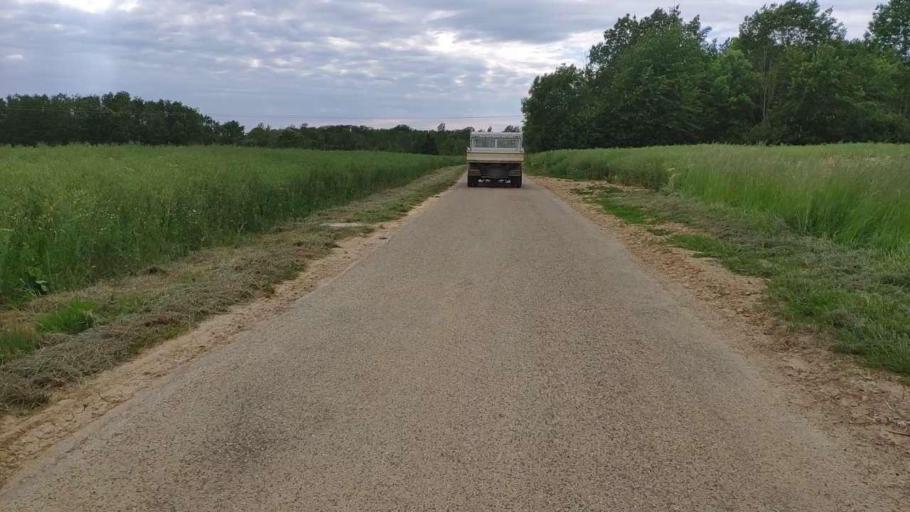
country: FR
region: Franche-Comte
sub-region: Departement du Jura
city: Bletterans
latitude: 46.8022
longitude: 5.5358
